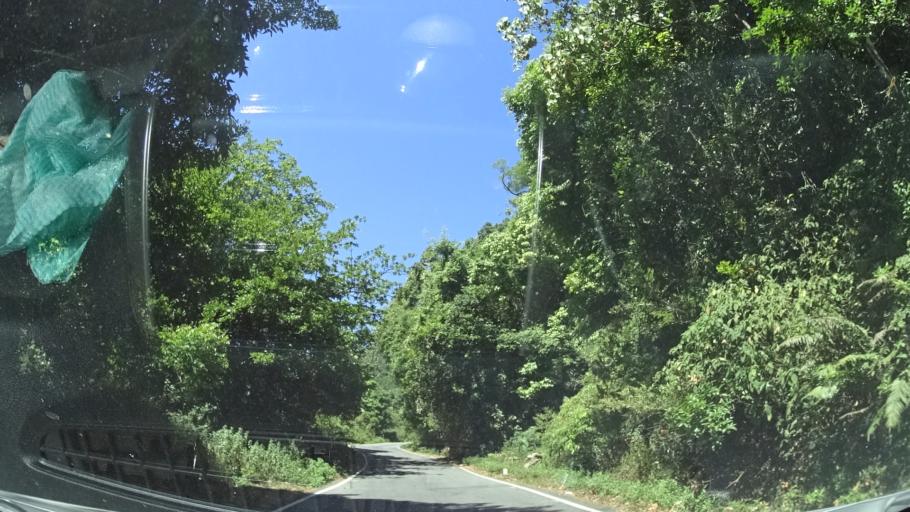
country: IN
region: Karnataka
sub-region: Udupi
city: Karkal
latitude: 13.2437
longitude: 75.1696
